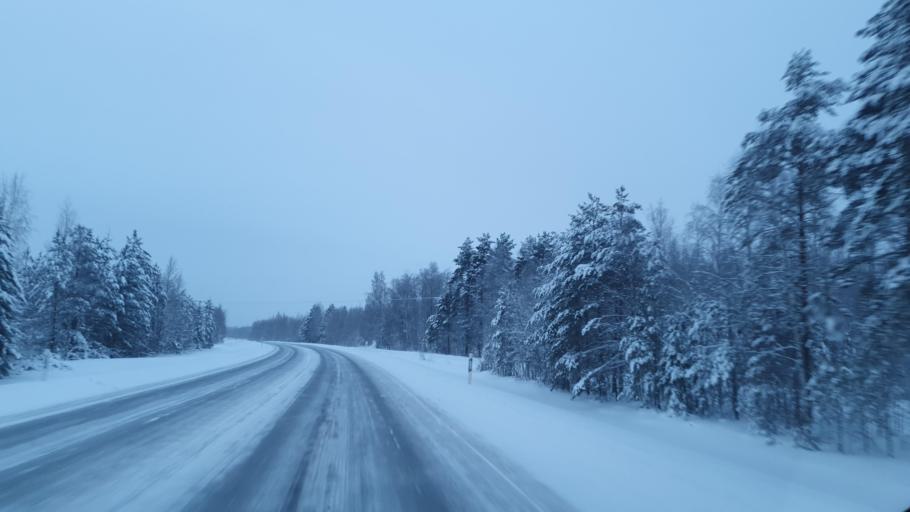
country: FI
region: Kainuu
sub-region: Kajaani
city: Vaala
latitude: 64.5932
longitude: 26.8004
